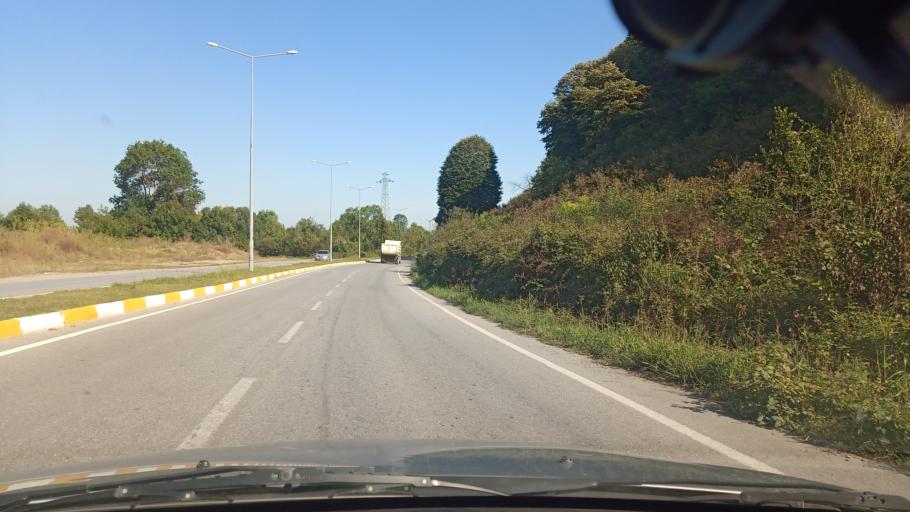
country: TR
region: Sakarya
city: Karasu
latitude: 41.1013
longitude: 30.6582
